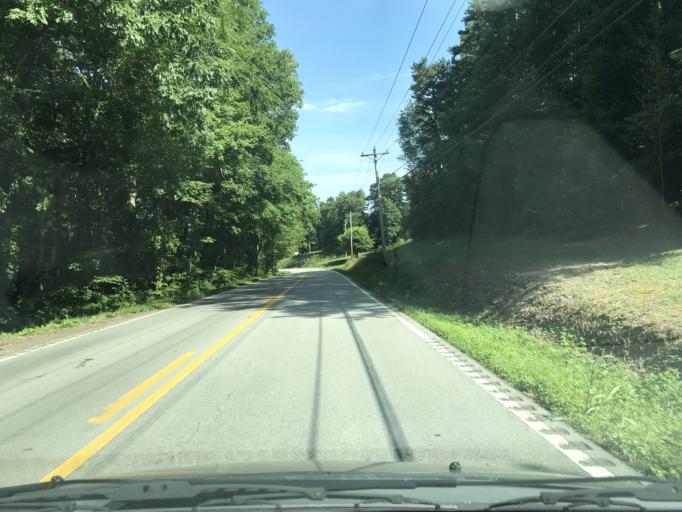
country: US
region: Tennessee
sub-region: Hamilton County
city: Lakesite
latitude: 35.2285
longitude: -85.0616
